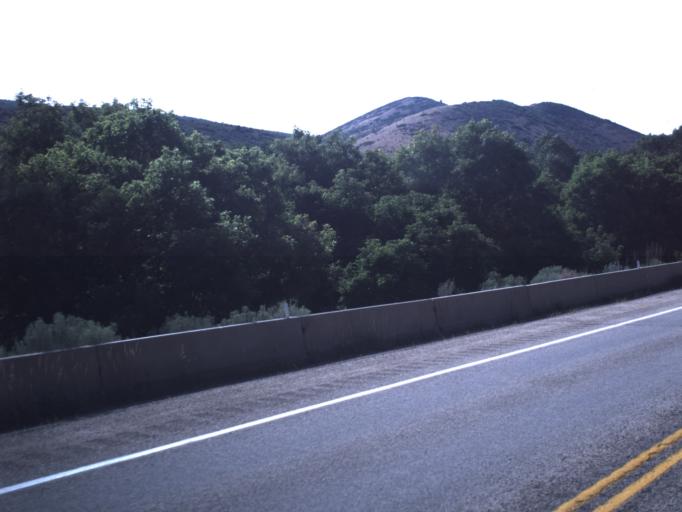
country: US
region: Utah
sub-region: Wasatch County
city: Heber
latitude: 40.4344
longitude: -111.3551
